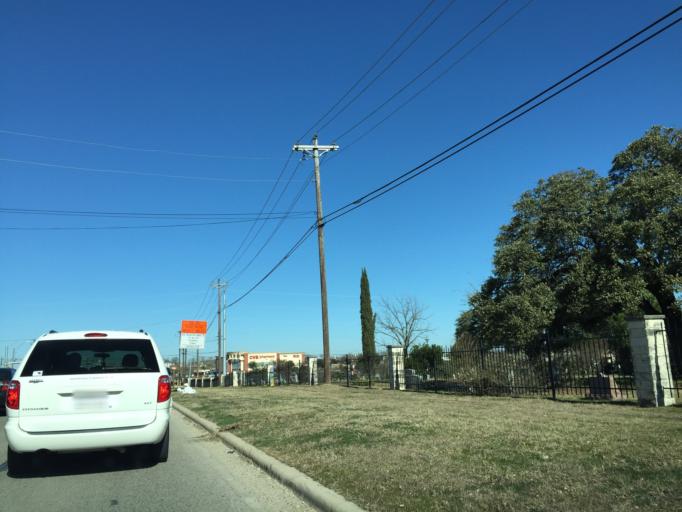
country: US
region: Texas
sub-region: Williamson County
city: Leander
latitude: 30.5753
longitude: -97.8714
